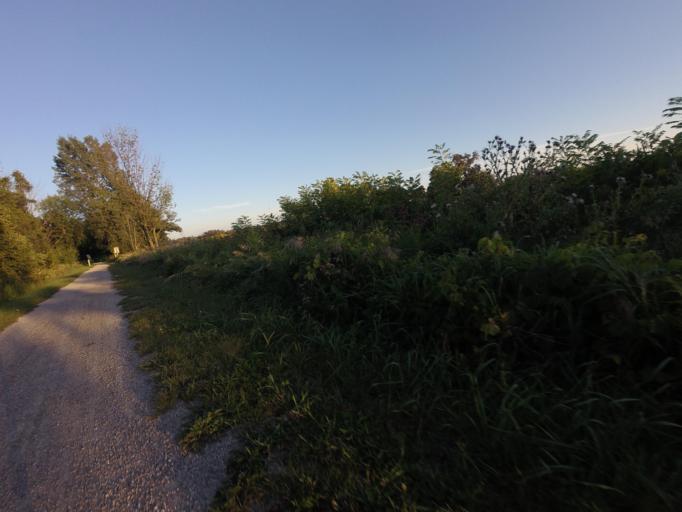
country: CA
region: Ontario
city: Goderich
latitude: 43.7568
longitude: -81.6811
